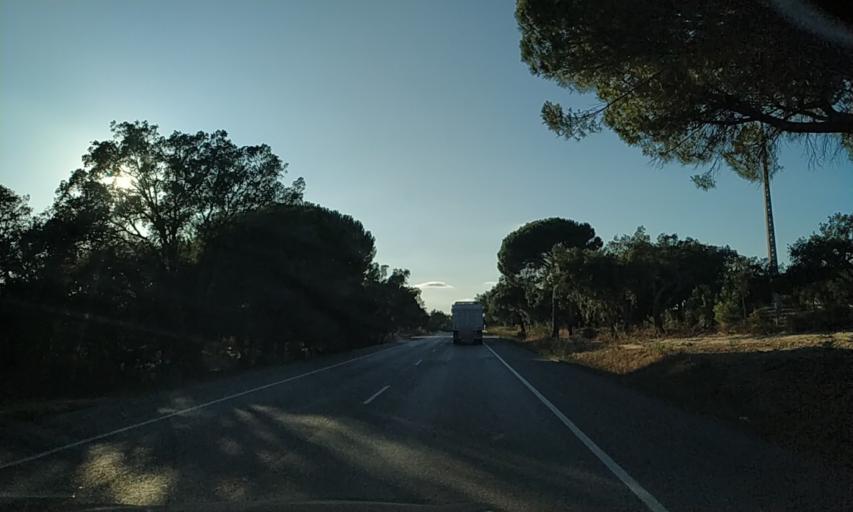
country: PT
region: Setubal
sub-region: Alcacer do Sal
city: Alcacer do Sal
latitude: 38.5353
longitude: -8.6350
